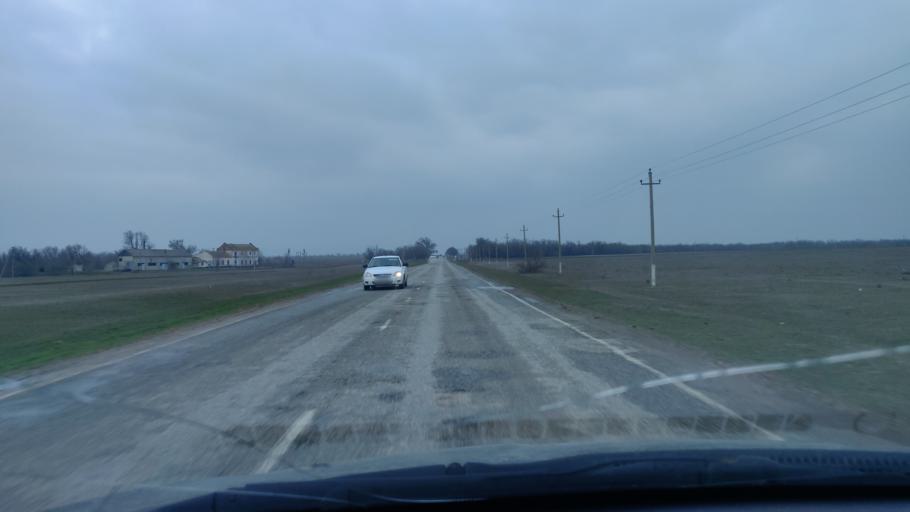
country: RU
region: Stavropol'skiy
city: Letnyaya Stavka
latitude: 45.3784
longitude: 43.3247
